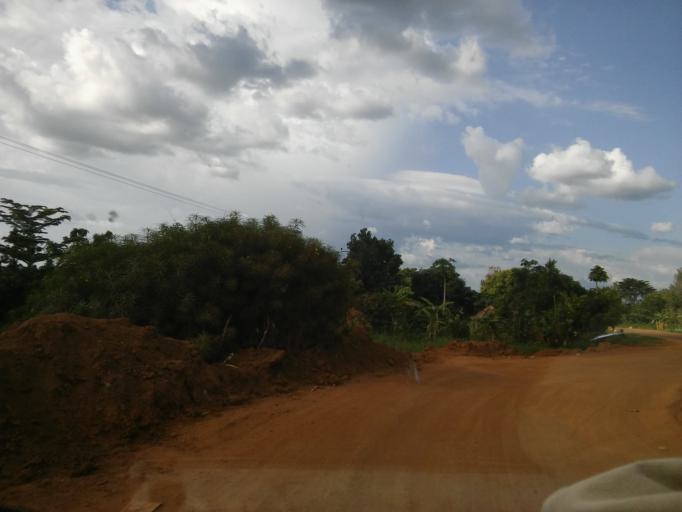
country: UG
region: Eastern Region
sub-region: Budaka District
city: Budaka
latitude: 1.0227
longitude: 33.9726
